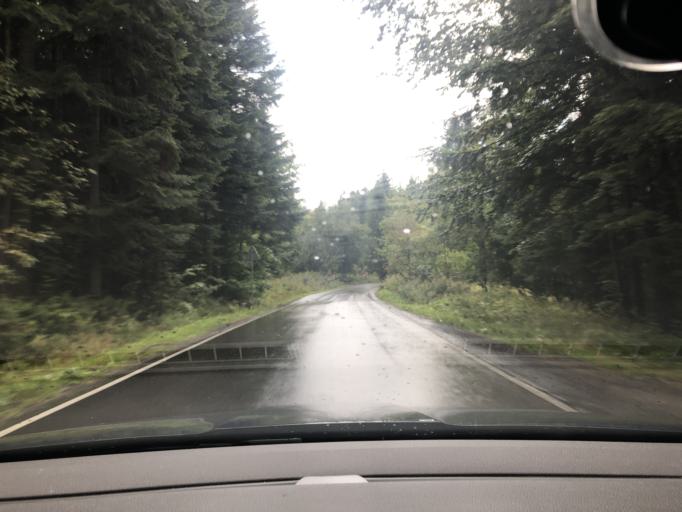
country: PL
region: Lesser Poland Voivodeship
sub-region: Powiat suski
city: Zawoja
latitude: 49.6856
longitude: 19.5604
